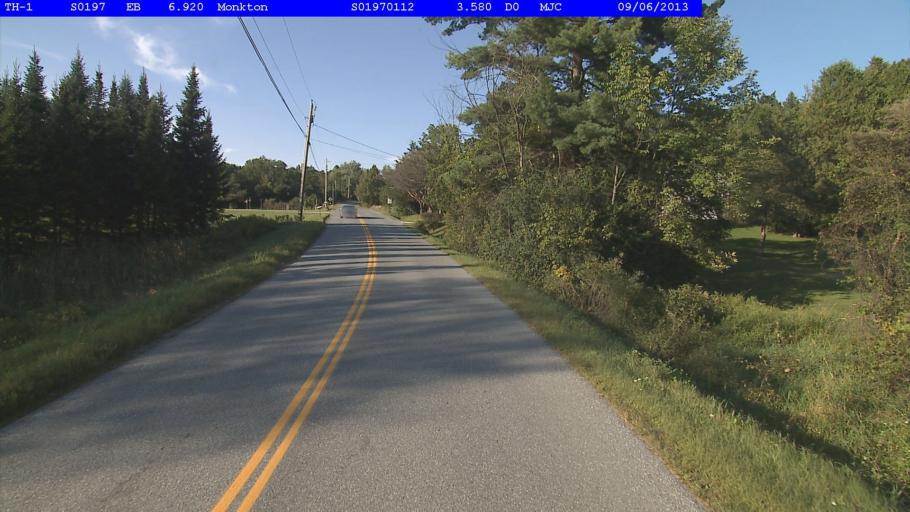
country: US
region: Vermont
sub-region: Chittenden County
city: Hinesburg
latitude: 44.2285
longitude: -73.1518
